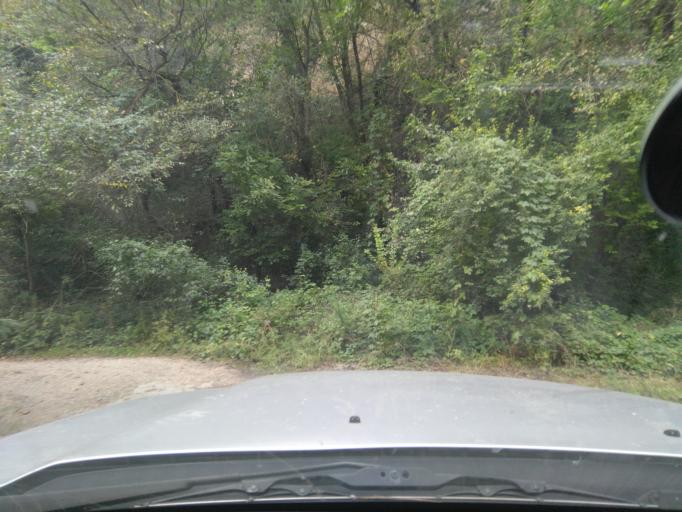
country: HU
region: Bacs-Kiskun
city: Apostag
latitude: 46.8954
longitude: 18.9399
